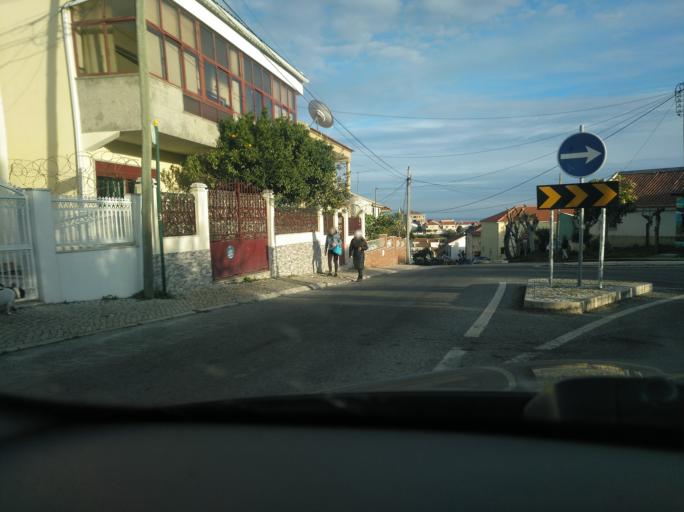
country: PT
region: Lisbon
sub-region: Loures
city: Unhos
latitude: 38.8155
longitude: -9.1219
